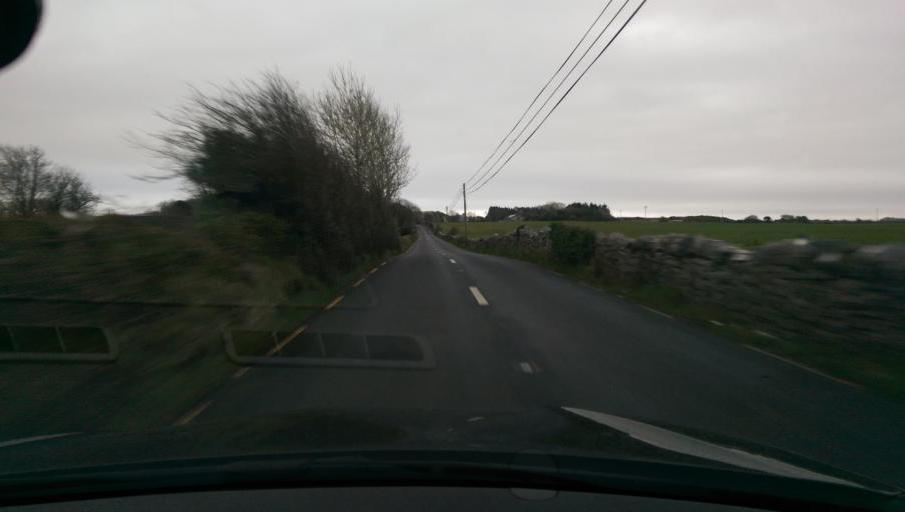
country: IE
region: Connaught
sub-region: County Galway
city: Athenry
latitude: 53.3099
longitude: -8.7949
